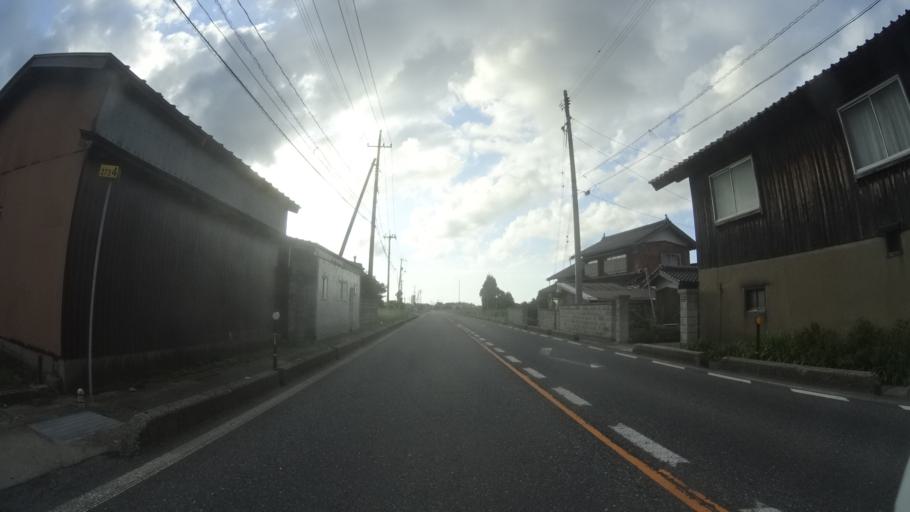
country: JP
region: Tottori
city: Kurayoshi
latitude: 35.5224
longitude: 133.5967
